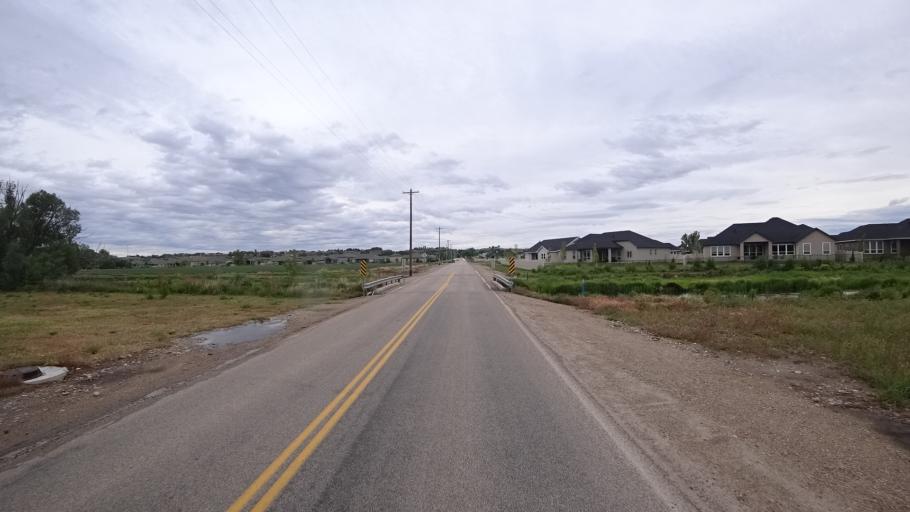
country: US
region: Idaho
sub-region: Ada County
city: Star
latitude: 43.7073
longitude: -116.5033
